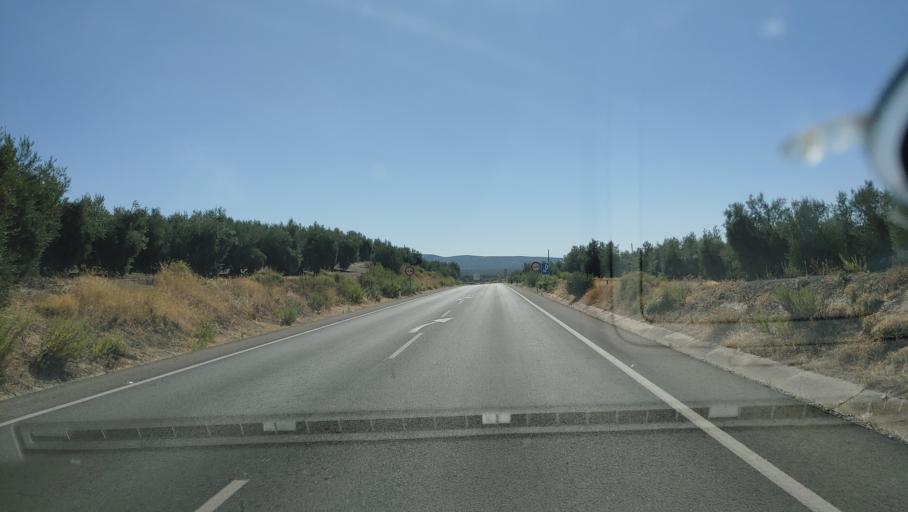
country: ES
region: Andalusia
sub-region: Provincia de Jaen
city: Campina
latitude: 38.2222
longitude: -2.9721
